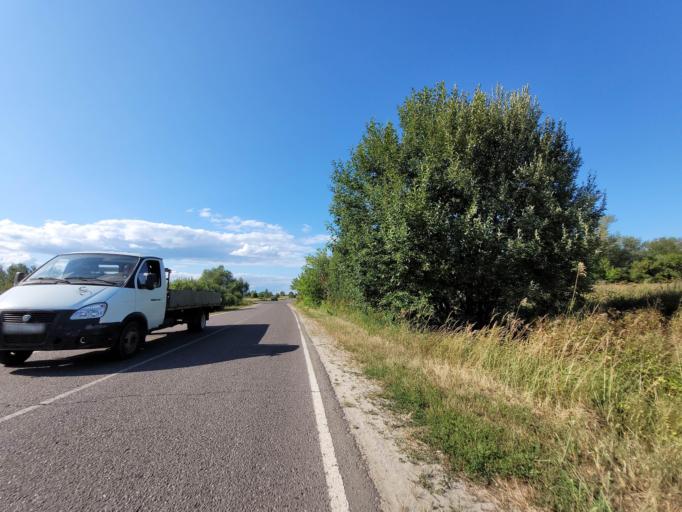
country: RU
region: Moskovskaya
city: Konobeyevo
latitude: 55.4036
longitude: 38.7081
